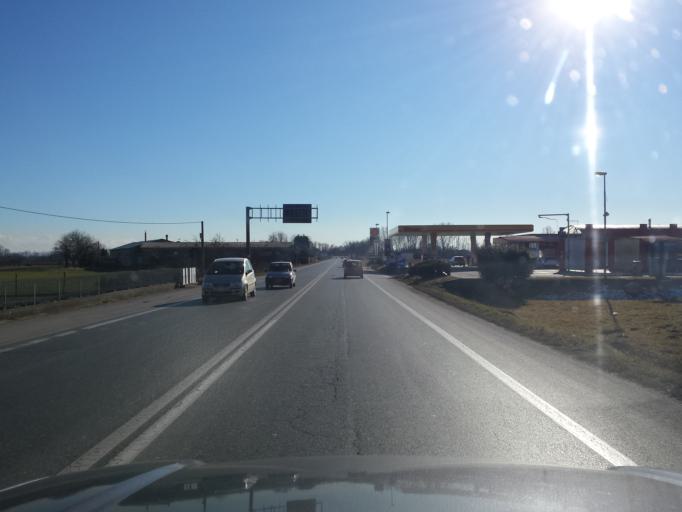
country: IT
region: Piedmont
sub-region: Provincia di Torino
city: Ozegna
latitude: 45.3446
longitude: 7.7415
